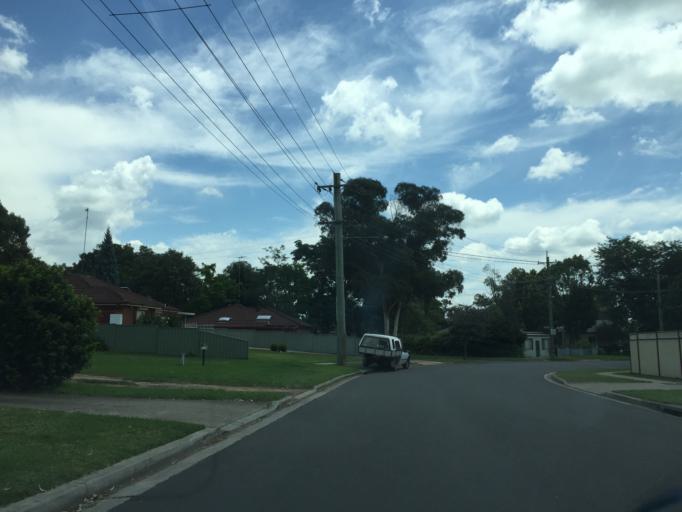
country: AU
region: New South Wales
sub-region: Blacktown
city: Riverstone
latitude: -33.6986
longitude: 150.8693
